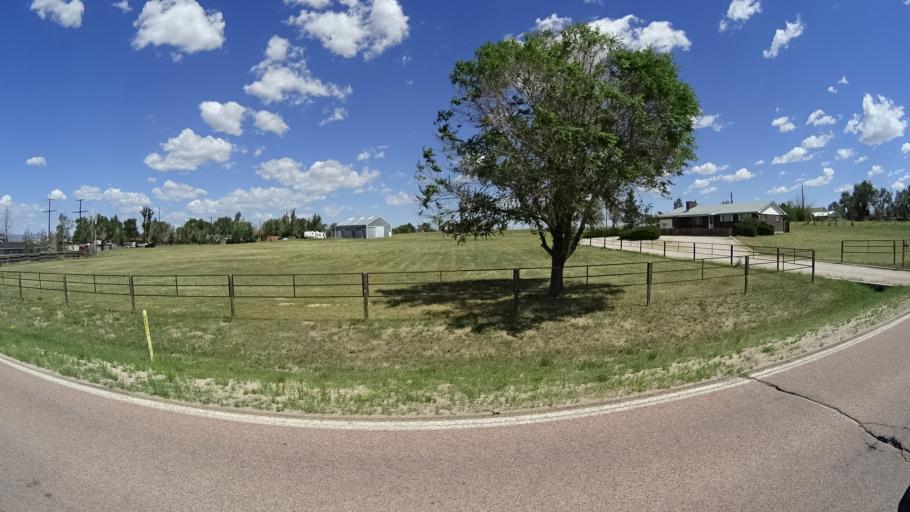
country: US
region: Colorado
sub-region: El Paso County
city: Cimarron Hills
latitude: 38.9115
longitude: -104.6244
